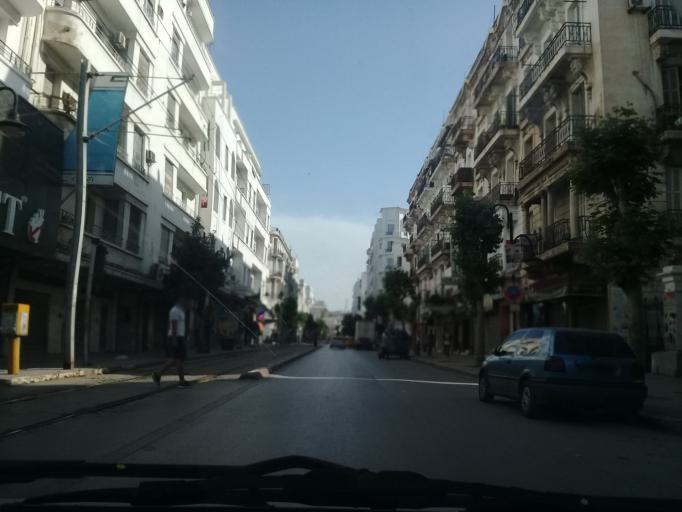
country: TN
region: Tunis
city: Tunis
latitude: 36.8042
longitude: 10.1798
